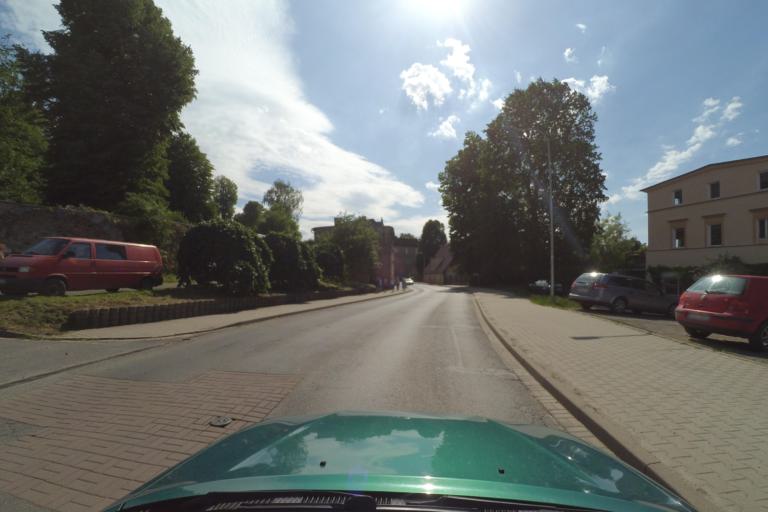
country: PL
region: Lower Silesian Voivodeship
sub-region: Powiat kamiennogorski
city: Kamienna Gora
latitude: 50.7860
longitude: 16.0388
